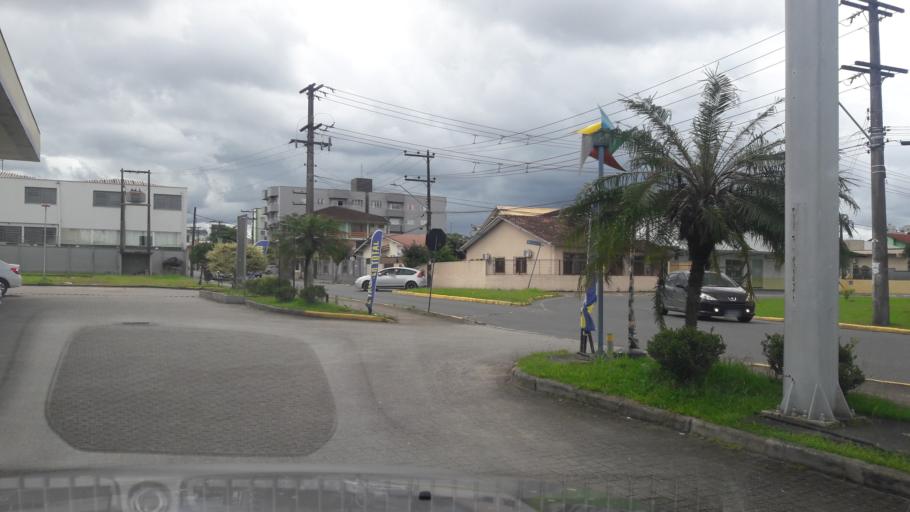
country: BR
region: Santa Catarina
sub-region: Joinville
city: Joinville
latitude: -26.3209
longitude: -48.8400
